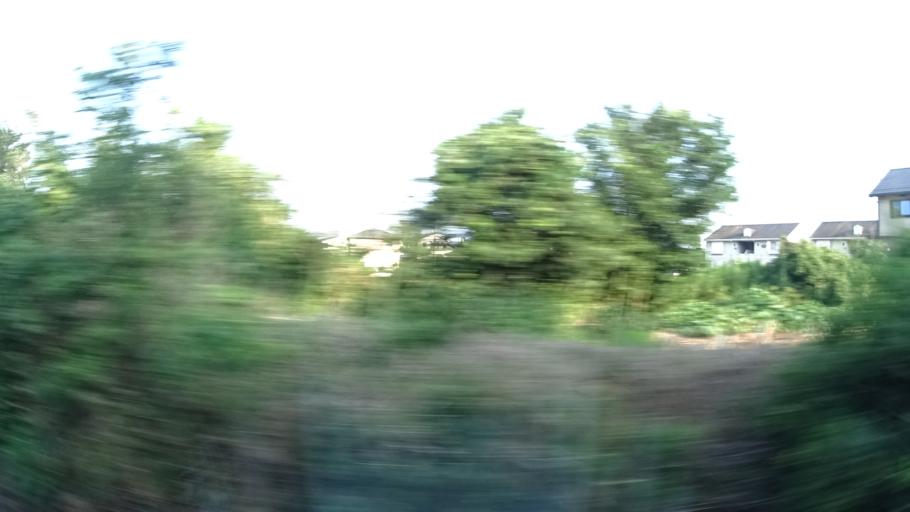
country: JP
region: Ibaraki
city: Funaishikawa
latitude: 36.4741
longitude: 140.5773
